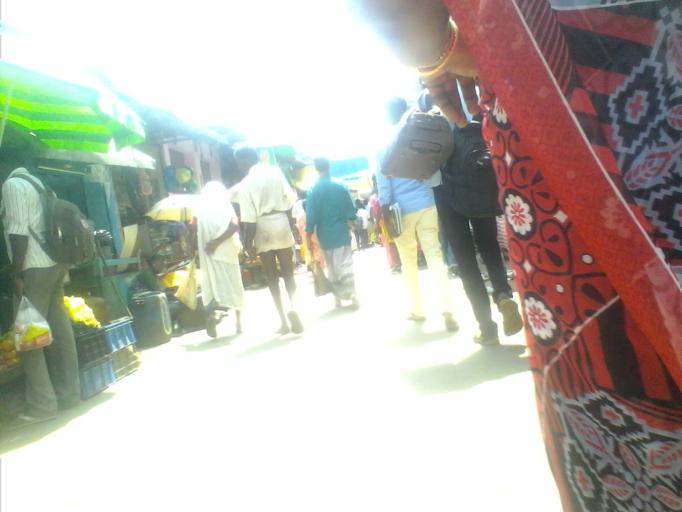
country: IN
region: Tamil Nadu
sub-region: Nagapattinam
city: Mayiladuthurai
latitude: 11.1015
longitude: 79.6505
